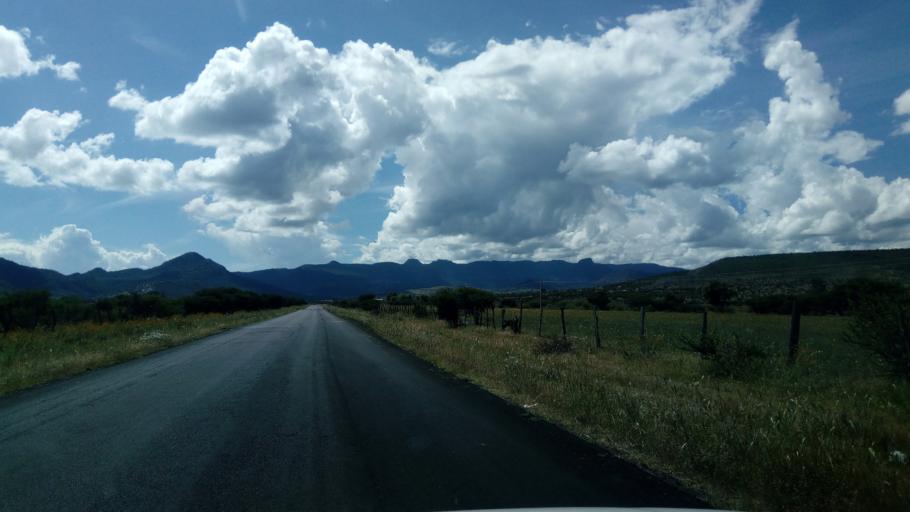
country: MX
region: Durango
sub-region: Durango
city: Jose Refugio Salcido
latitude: 23.8061
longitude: -104.4841
